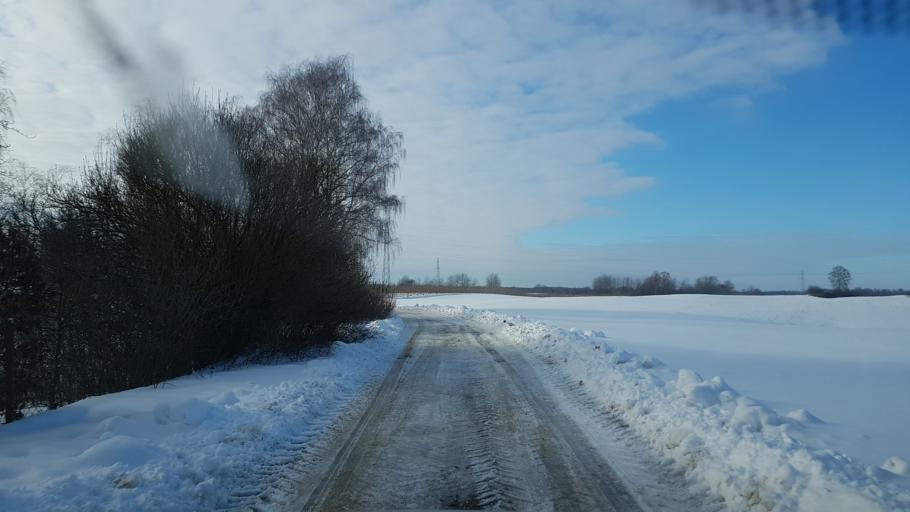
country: PL
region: West Pomeranian Voivodeship
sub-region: Powiat drawski
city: Drawsko Pomorskie
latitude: 53.5386
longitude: 15.7808
